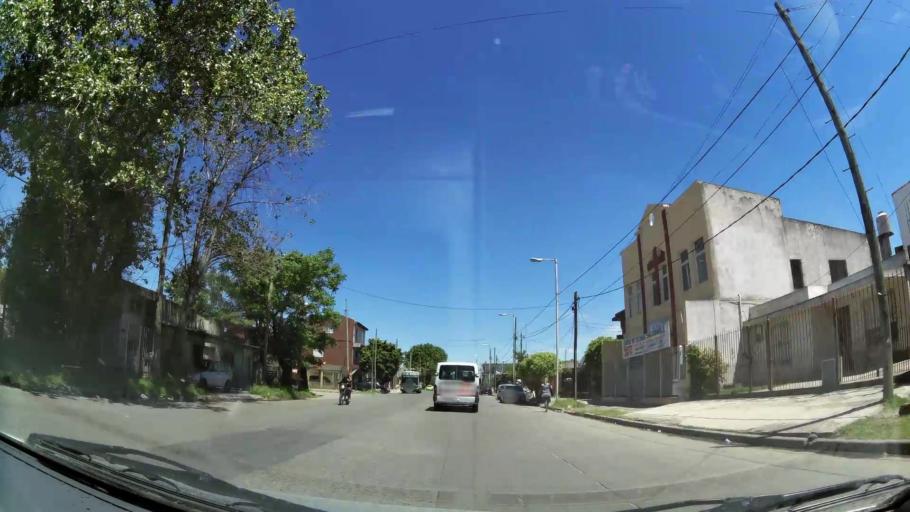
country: AR
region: Buenos Aires
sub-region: Partido de Quilmes
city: Quilmes
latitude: -34.7156
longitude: -58.3214
